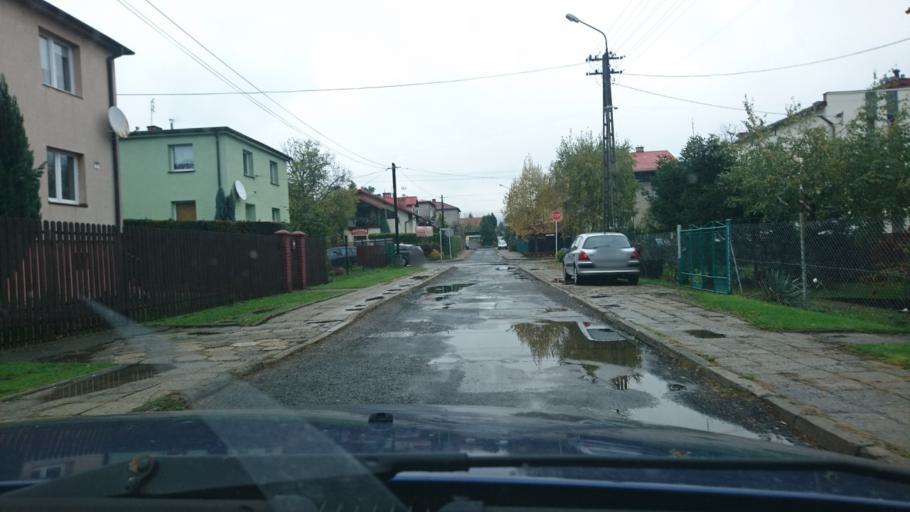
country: PL
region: Silesian Voivodeship
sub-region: Bielsko-Biala
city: Bielsko-Biala
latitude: 49.8031
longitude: 19.0635
